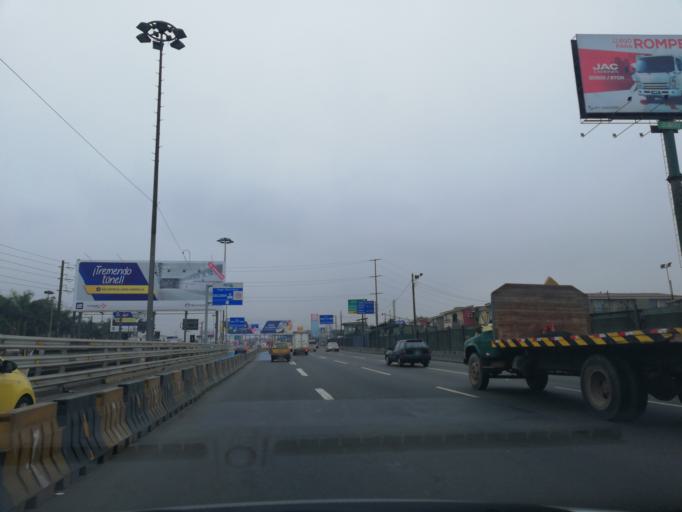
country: PE
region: Lima
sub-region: Lima
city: San Luis
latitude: -12.0693
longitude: -76.9722
